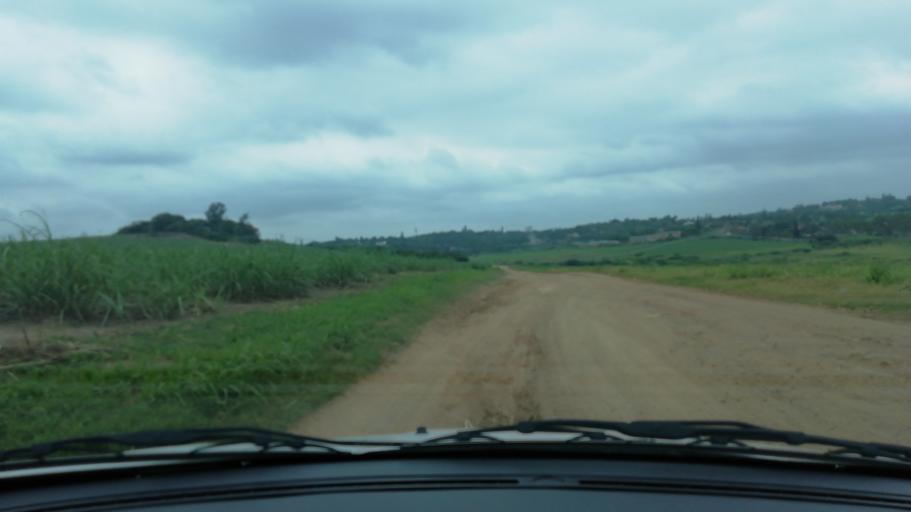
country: ZA
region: KwaZulu-Natal
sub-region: uThungulu District Municipality
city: Empangeni
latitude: -28.7335
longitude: 31.9082
